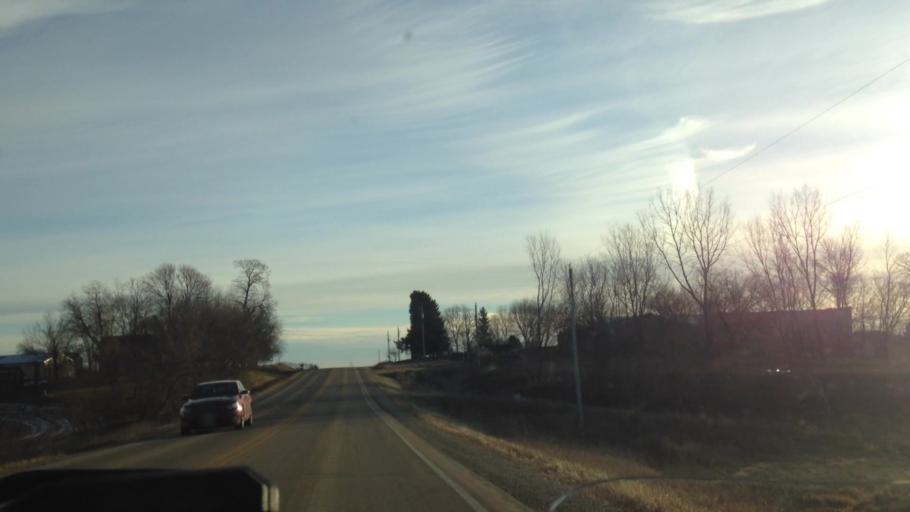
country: US
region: Wisconsin
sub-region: Dodge County
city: Theresa
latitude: 43.5364
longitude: -88.4689
